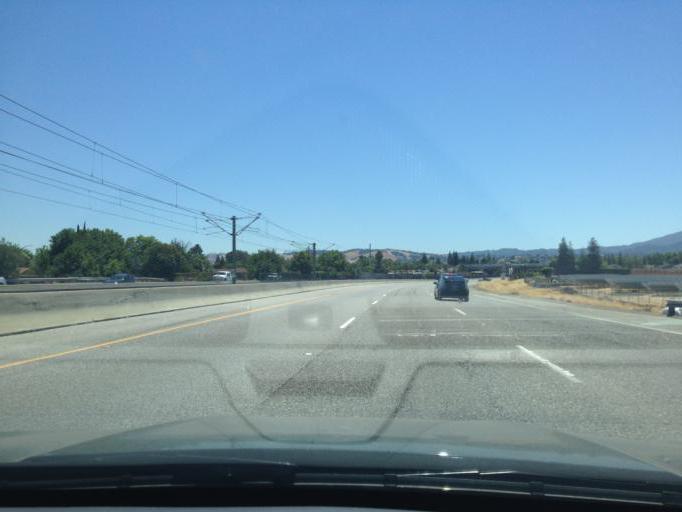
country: US
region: California
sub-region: Santa Clara County
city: Seven Trees
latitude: 37.2702
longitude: -121.8610
